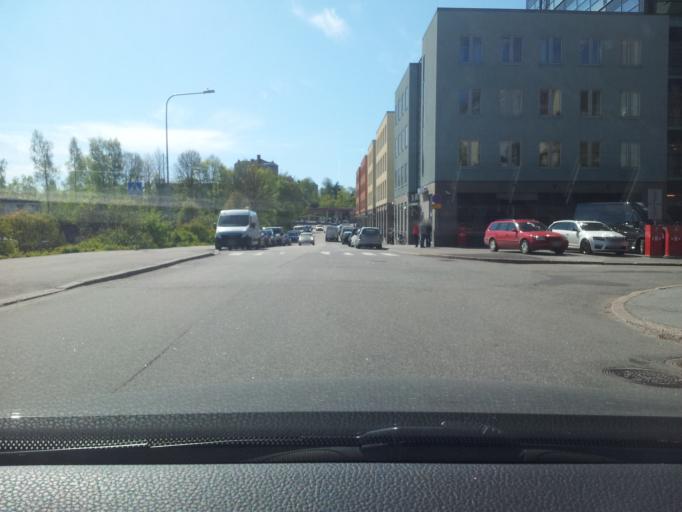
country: FI
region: Uusimaa
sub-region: Helsinki
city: Helsinki
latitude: 60.2047
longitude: 24.9003
